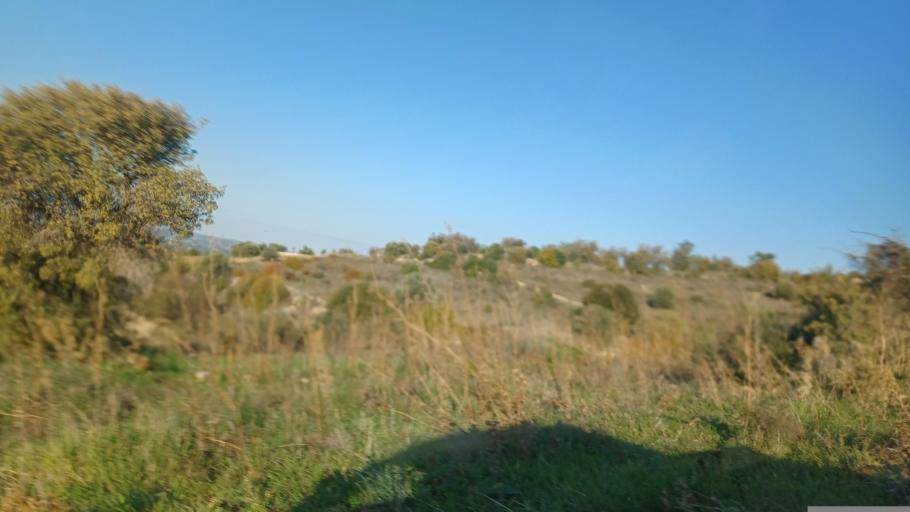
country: CY
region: Pafos
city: Mesogi
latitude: 34.8700
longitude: 32.5809
